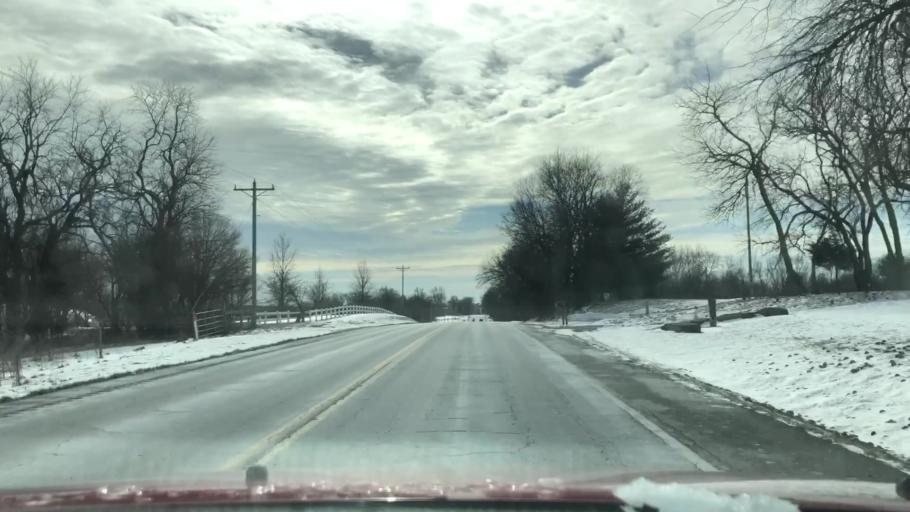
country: US
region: Missouri
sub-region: Jackson County
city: Lone Jack
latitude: 38.8782
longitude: -94.1352
